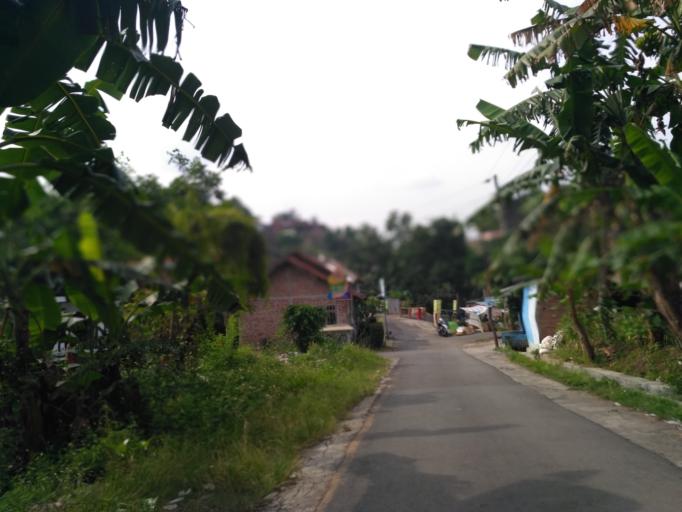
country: ID
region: Central Java
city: Semarang
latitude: -7.0211
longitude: 110.4419
